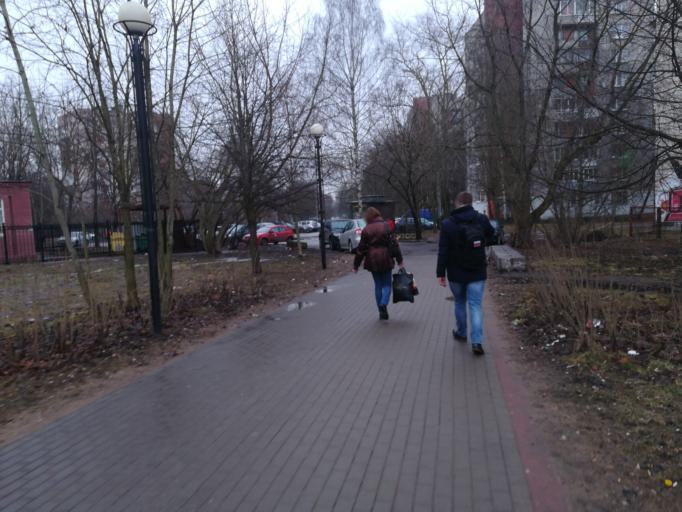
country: RU
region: St.-Petersburg
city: Vasyl'evsky Ostrov
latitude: 59.9493
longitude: 30.2368
